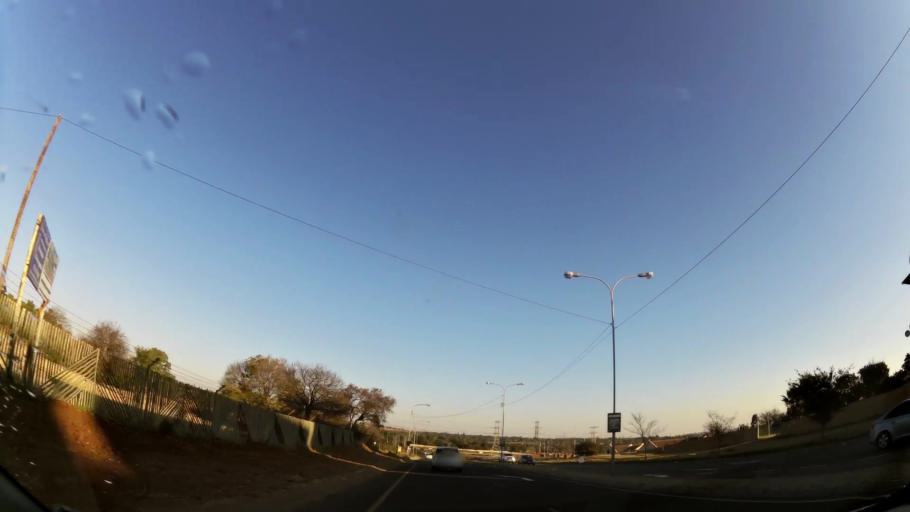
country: ZA
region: Gauteng
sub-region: City of Tshwane Metropolitan Municipality
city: Centurion
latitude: -25.8837
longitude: 28.1415
